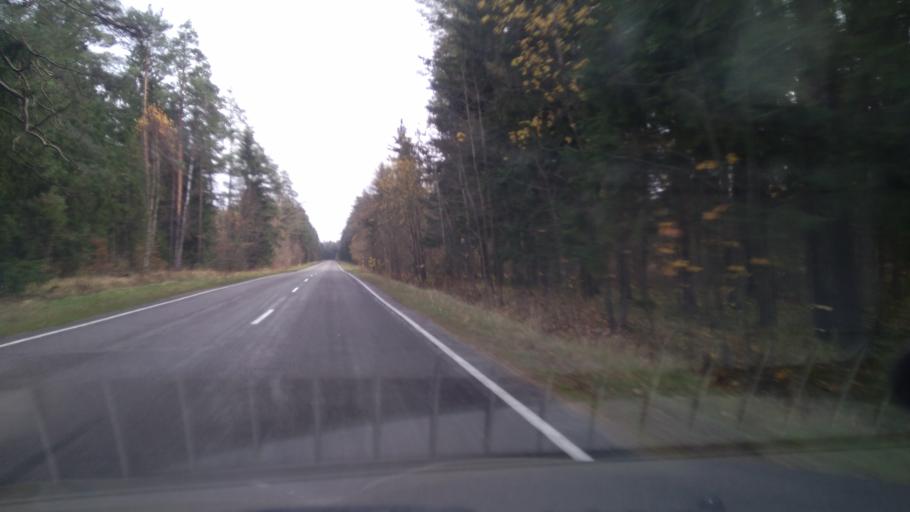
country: BY
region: Minsk
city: Urechcha
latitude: 53.2063
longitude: 27.7870
